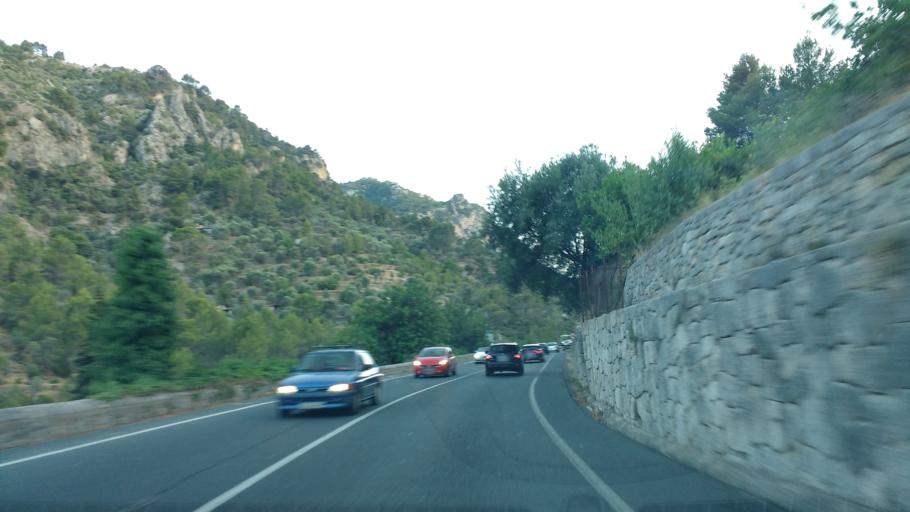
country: ES
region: Balearic Islands
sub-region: Illes Balears
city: Soller
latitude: 39.7579
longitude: 2.7110
